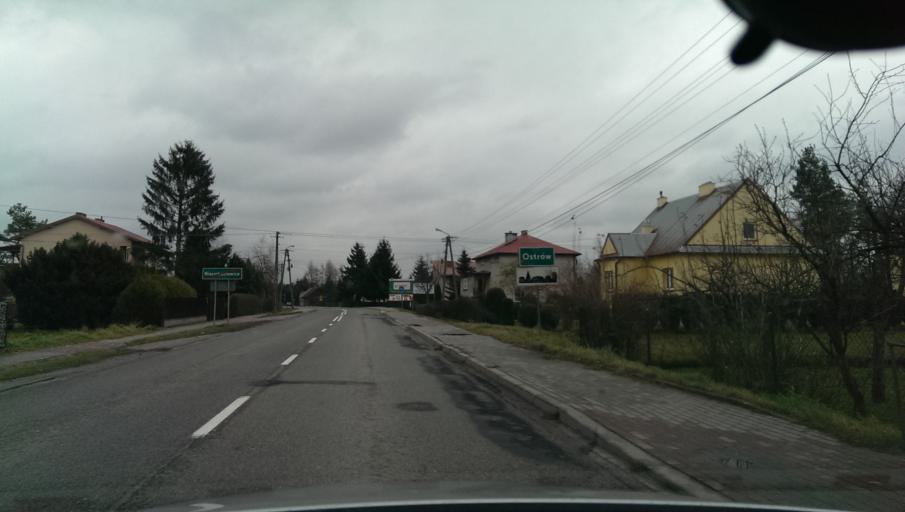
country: PL
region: Lesser Poland Voivodeship
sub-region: Powiat tarnowski
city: Wierzchoslawice
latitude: 50.0155
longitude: 20.8772
